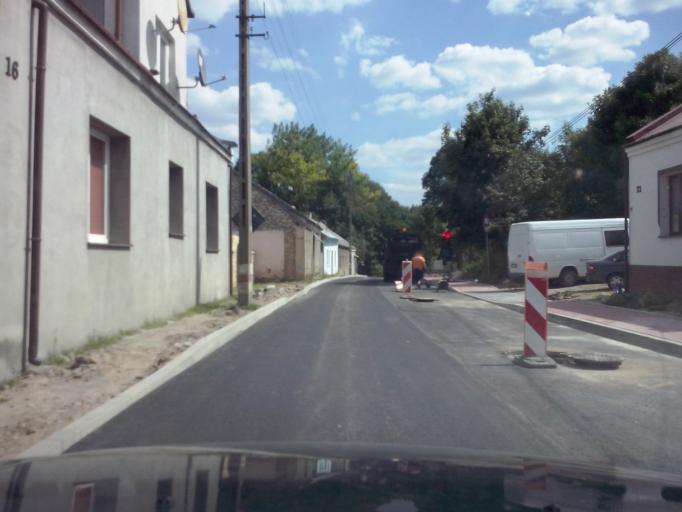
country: PL
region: Swietokrzyskie
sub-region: Powiat staszowski
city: Staszow
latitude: 50.5898
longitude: 21.1074
